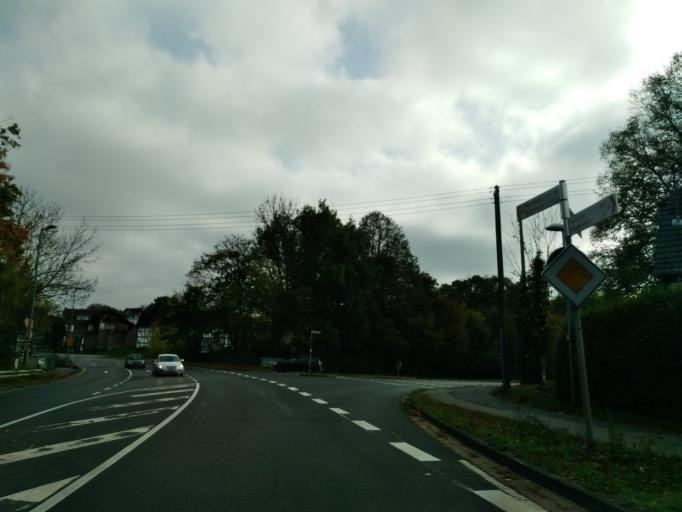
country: DE
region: North Rhine-Westphalia
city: Sankt Augustin
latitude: 50.7492
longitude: 7.2213
